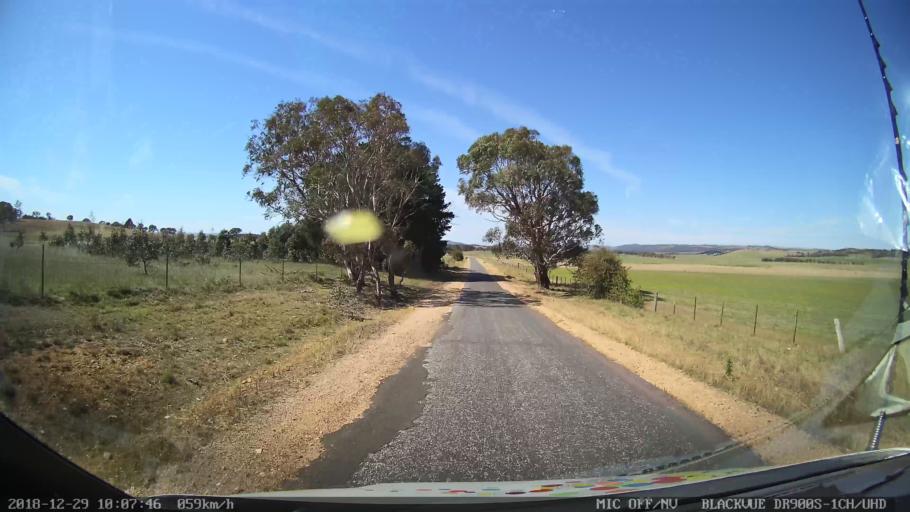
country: AU
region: New South Wales
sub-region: Yass Valley
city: Gundaroo
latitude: -34.8558
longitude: 149.4523
